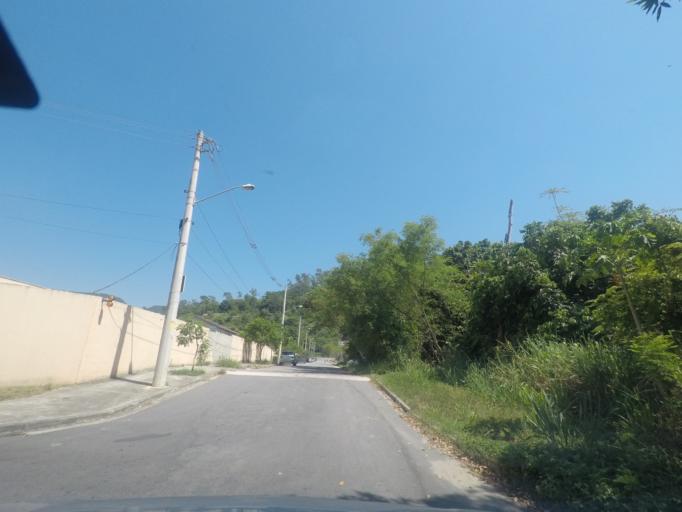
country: BR
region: Rio de Janeiro
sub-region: Nilopolis
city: Nilopolis
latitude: -22.9901
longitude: -43.4847
